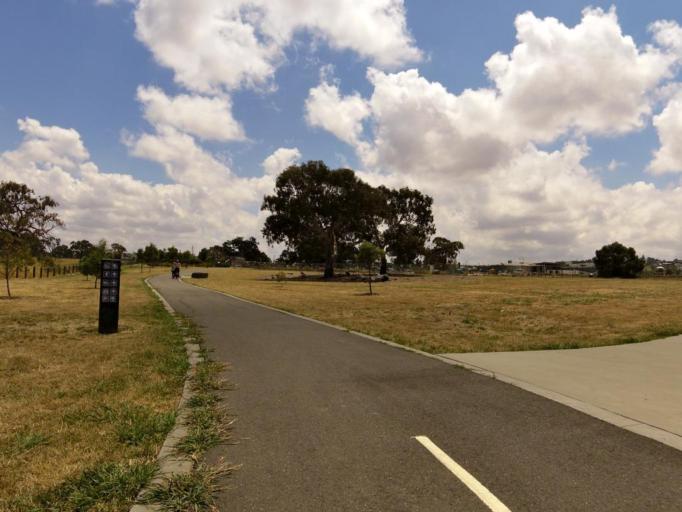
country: AU
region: Victoria
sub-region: Hume
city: Craigieburn
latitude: -37.5786
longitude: 144.9176
